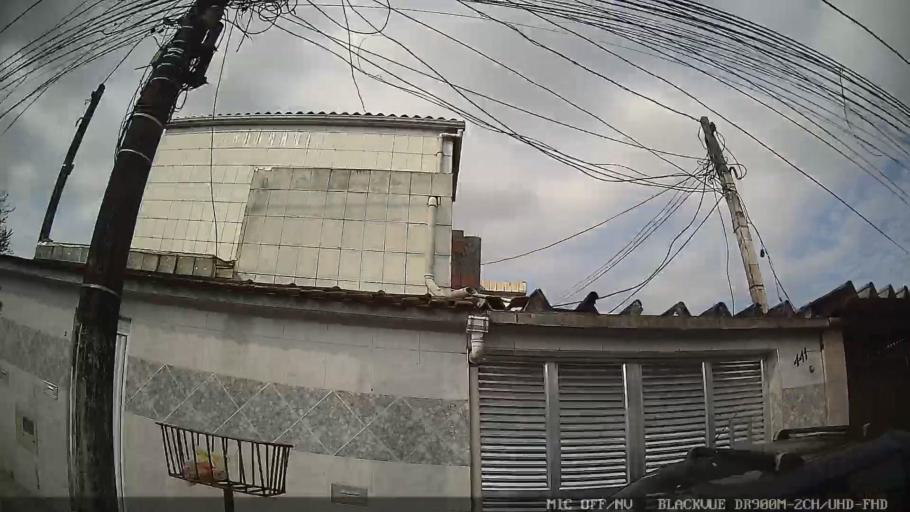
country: BR
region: Sao Paulo
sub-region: Santos
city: Santos
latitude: -23.9496
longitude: -46.2892
